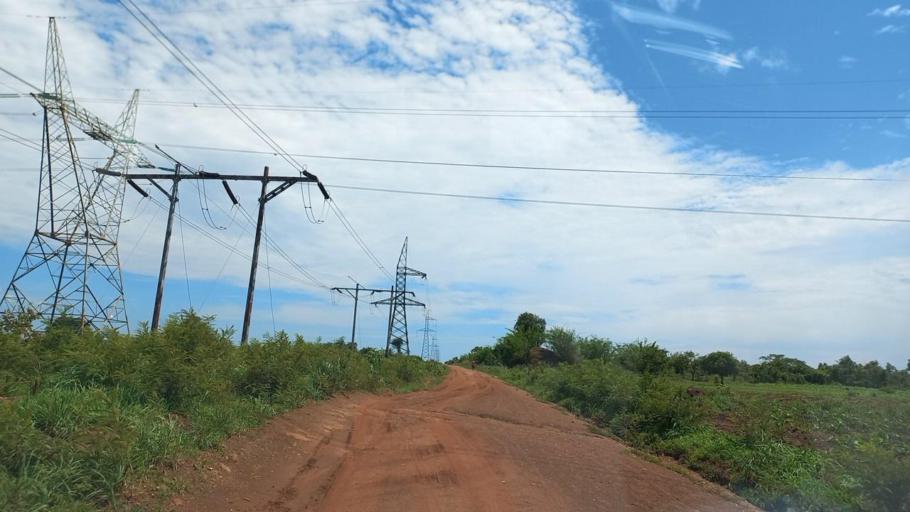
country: ZM
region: Copperbelt
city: Kitwe
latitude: -12.8523
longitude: 28.3321
